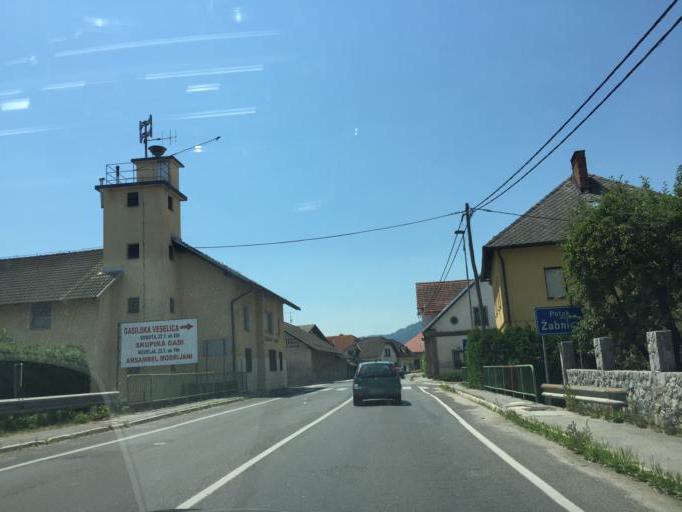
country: SI
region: Skofja Loka
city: Sv. Duh
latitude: 46.1964
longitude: 14.3319
